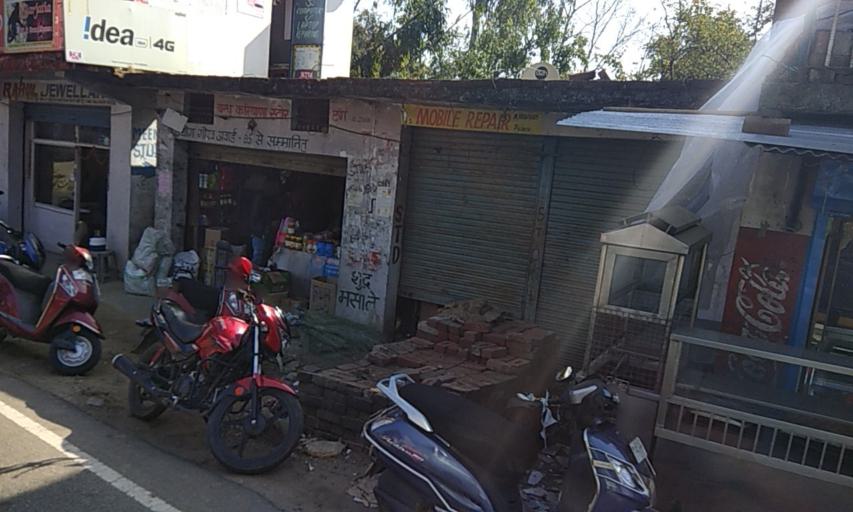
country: IN
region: Himachal Pradesh
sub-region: Kangra
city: Dharmsala
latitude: 32.1636
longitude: 76.4007
